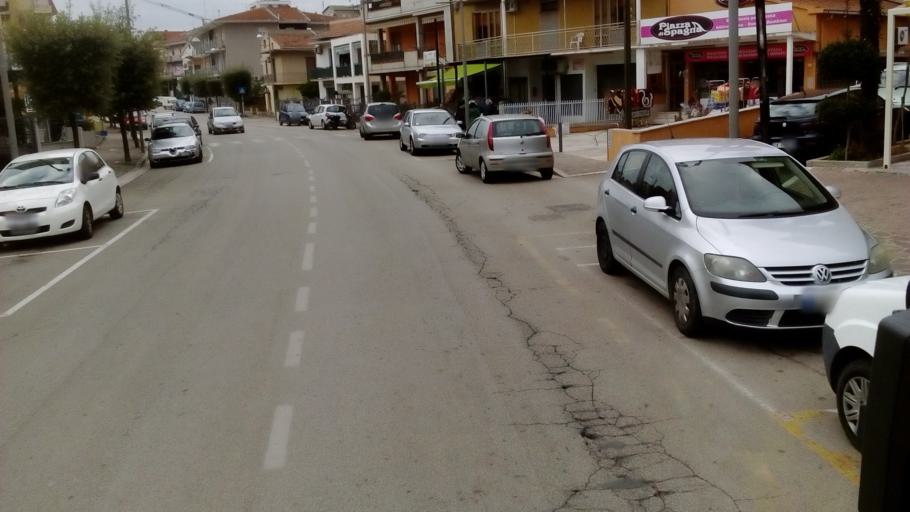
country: IT
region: Abruzzo
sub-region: Provincia di Chieti
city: San Salvo
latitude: 42.0542
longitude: 14.7334
